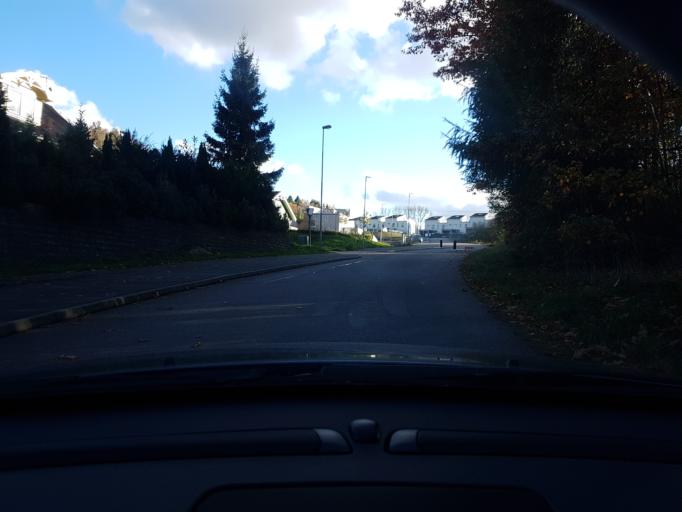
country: SE
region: Vaestra Goetaland
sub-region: Ale Kommun
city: Surte
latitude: 57.8185
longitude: 12.0253
